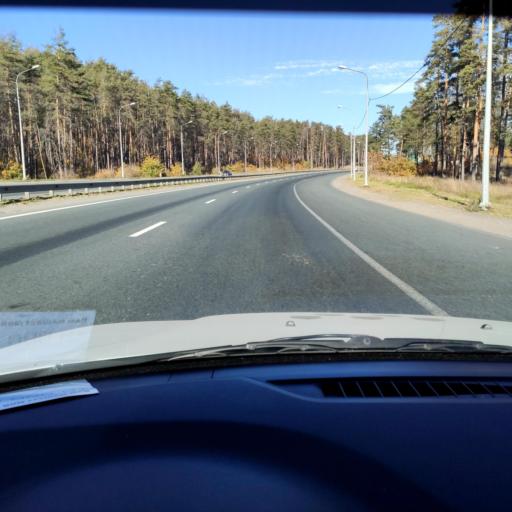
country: RU
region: Samara
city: Zhigulevsk
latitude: 53.5330
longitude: 49.5171
